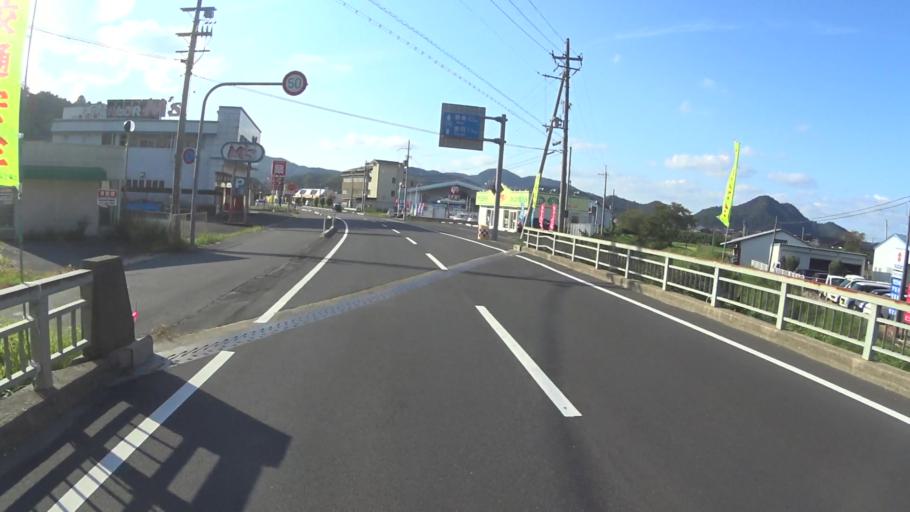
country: JP
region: Hyogo
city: Toyooka
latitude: 35.6015
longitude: 134.9011
